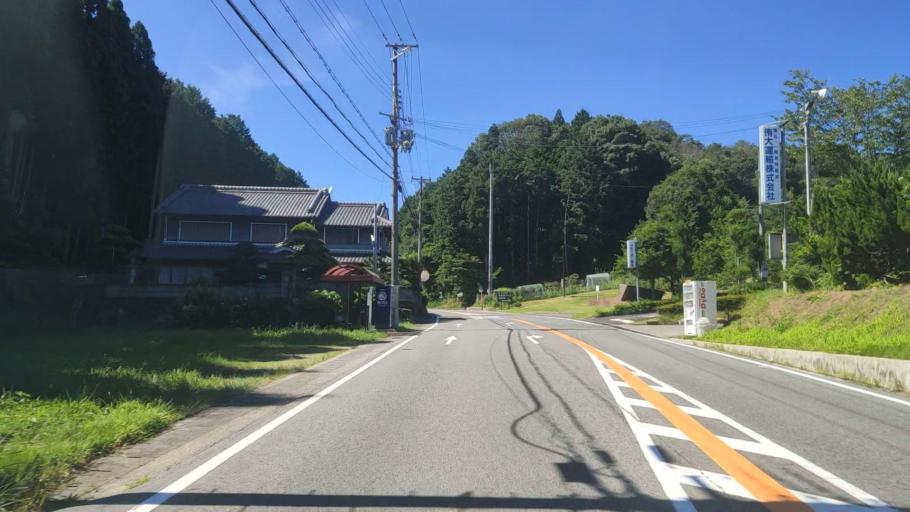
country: JP
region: Nara
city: Haibara-akanedai
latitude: 34.4581
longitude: 135.9344
